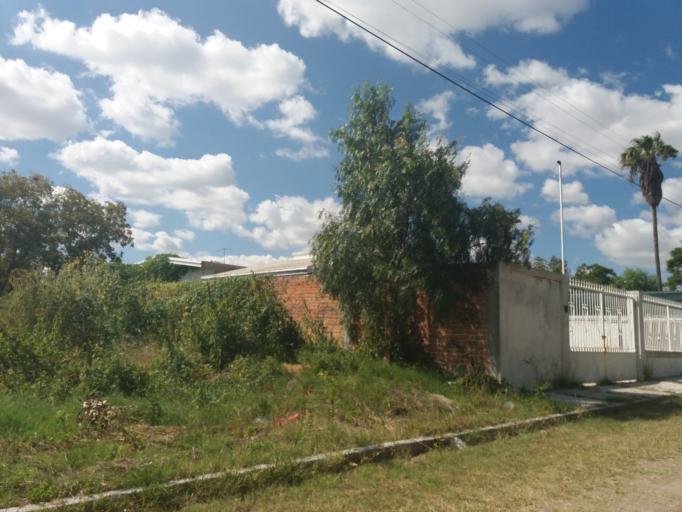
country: MX
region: Aguascalientes
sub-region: Aguascalientes
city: San Sebastian [Fraccionamiento]
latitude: 21.7913
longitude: -102.2774
